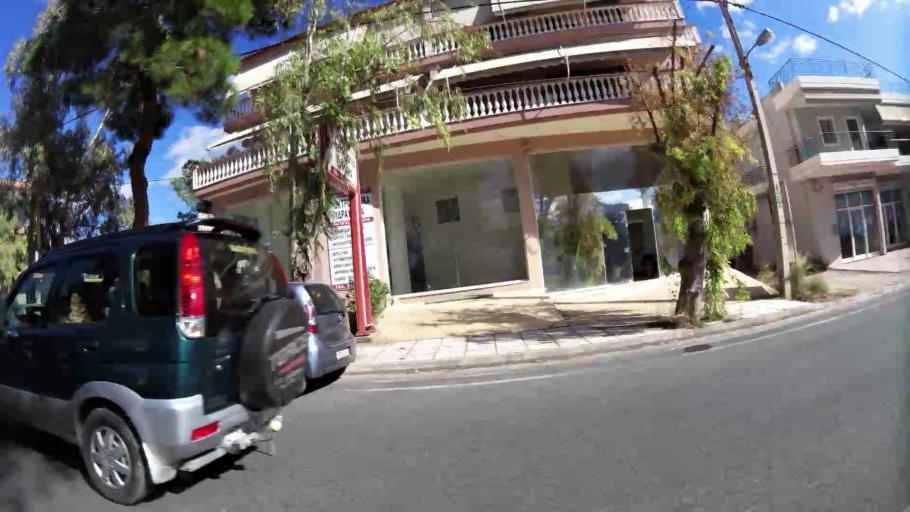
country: GR
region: Attica
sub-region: Nomarchia Anatolikis Attikis
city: Acharnes
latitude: 38.0996
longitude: 23.7375
